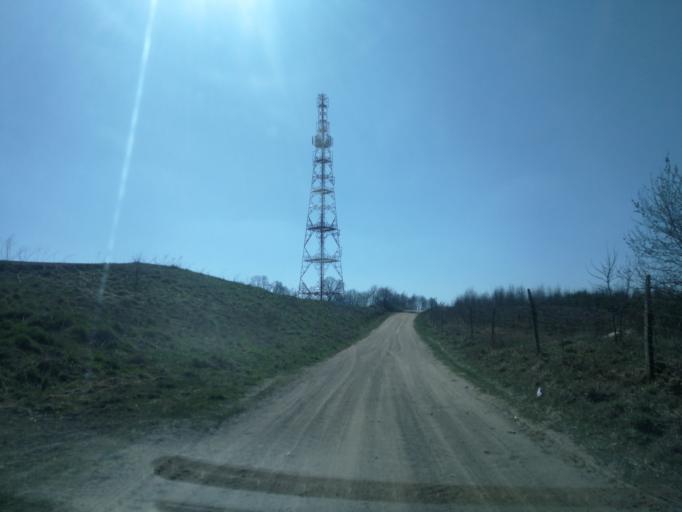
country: PL
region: Warmian-Masurian Voivodeship
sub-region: Powiat ostrodzki
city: Dabrowno
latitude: 53.4400
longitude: 19.9805
